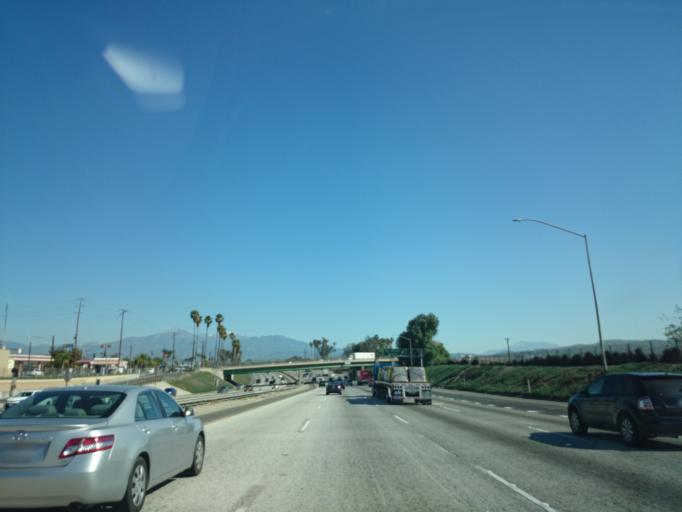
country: US
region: California
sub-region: San Bernardino County
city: Colton
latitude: 34.0650
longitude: -117.3163
